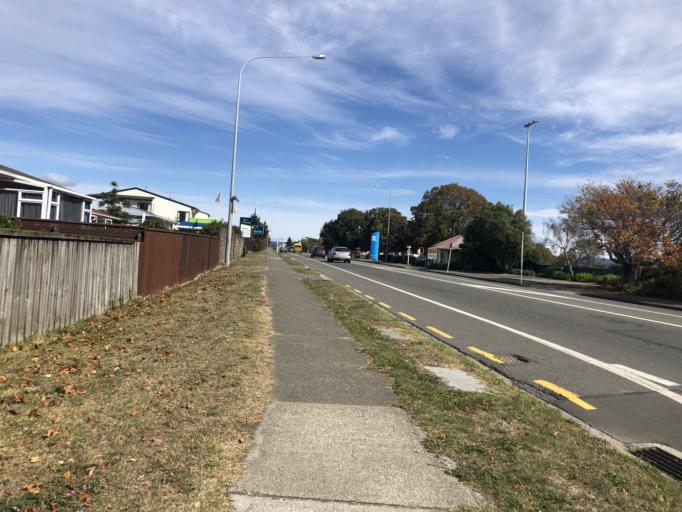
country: NZ
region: Tasman
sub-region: Tasman District
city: Richmond
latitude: -41.3390
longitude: 173.1781
